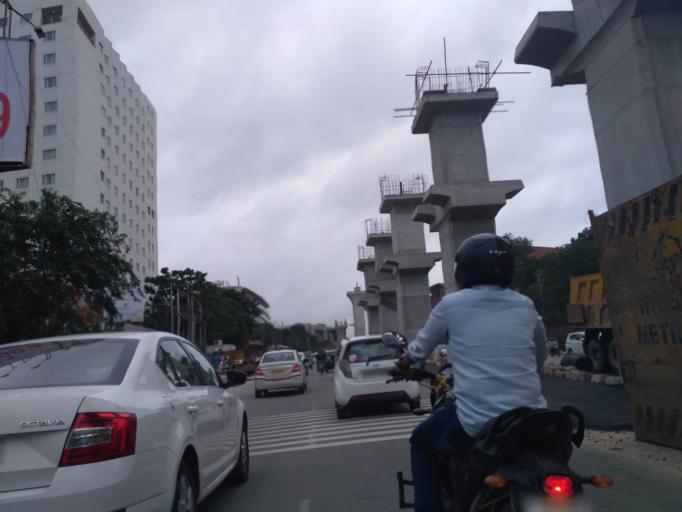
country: IN
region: Telangana
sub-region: Rangareddi
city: Kukatpalli
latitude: 17.4422
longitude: 78.3771
